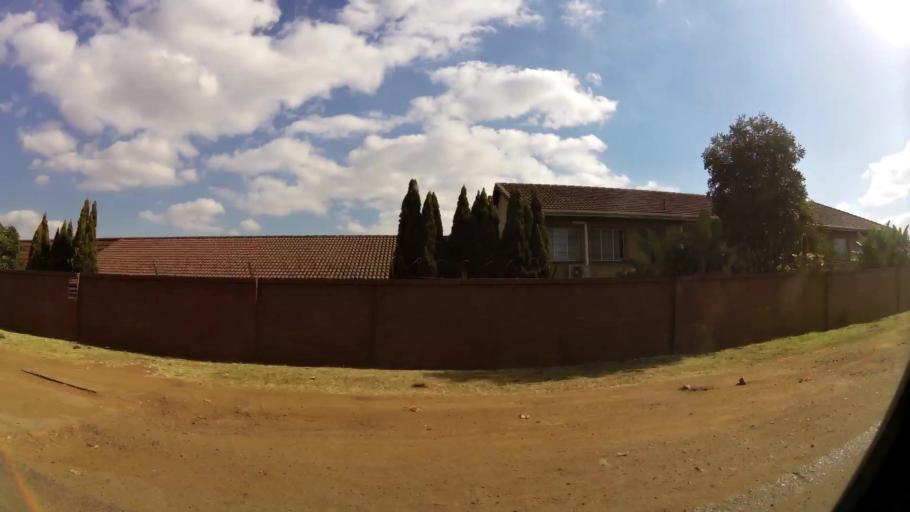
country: ZA
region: Gauteng
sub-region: Ekurhuleni Metropolitan Municipality
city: Tembisa
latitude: -25.9630
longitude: 28.2310
